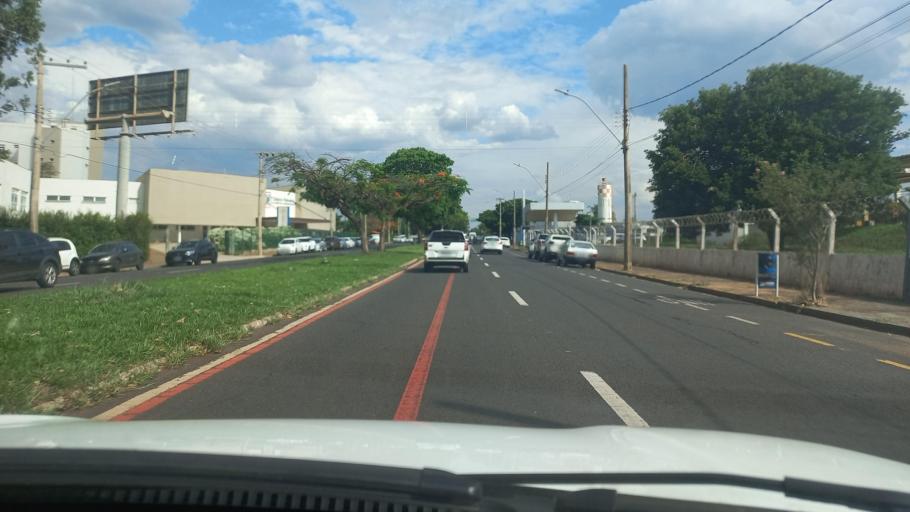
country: BR
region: Minas Gerais
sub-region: Uberaba
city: Uberaba
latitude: -19.7634
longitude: -47.9628
